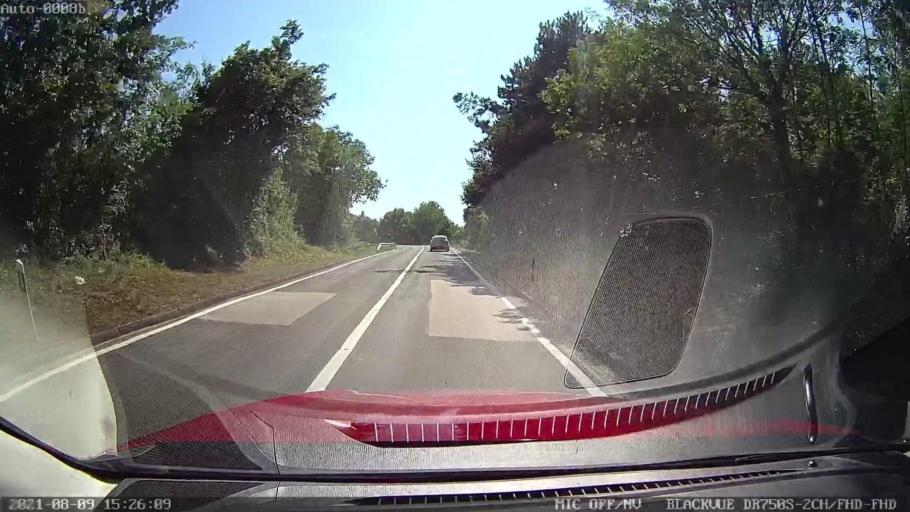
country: HR
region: Istarska
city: Pazin
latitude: 45.1642
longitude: 13.9080
